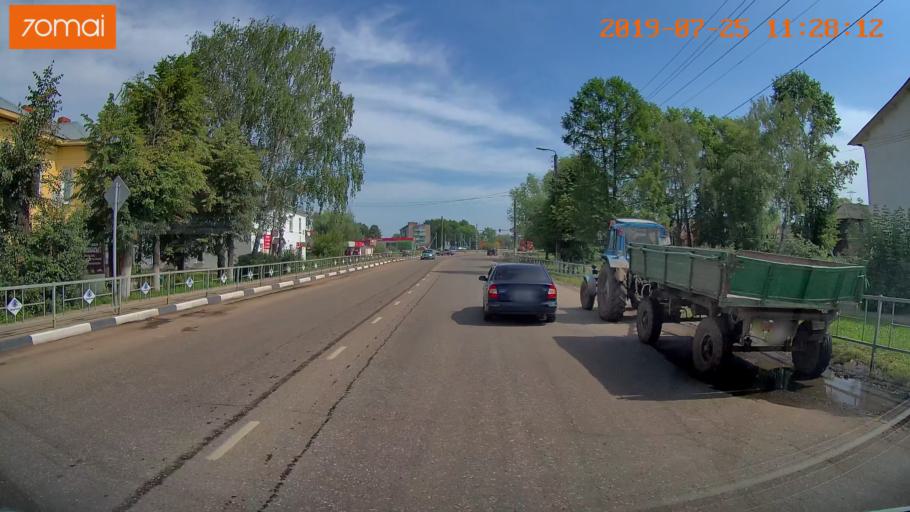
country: RU
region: Ivanovo
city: Privolzhsk
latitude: 57.3797
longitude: 41.2916
